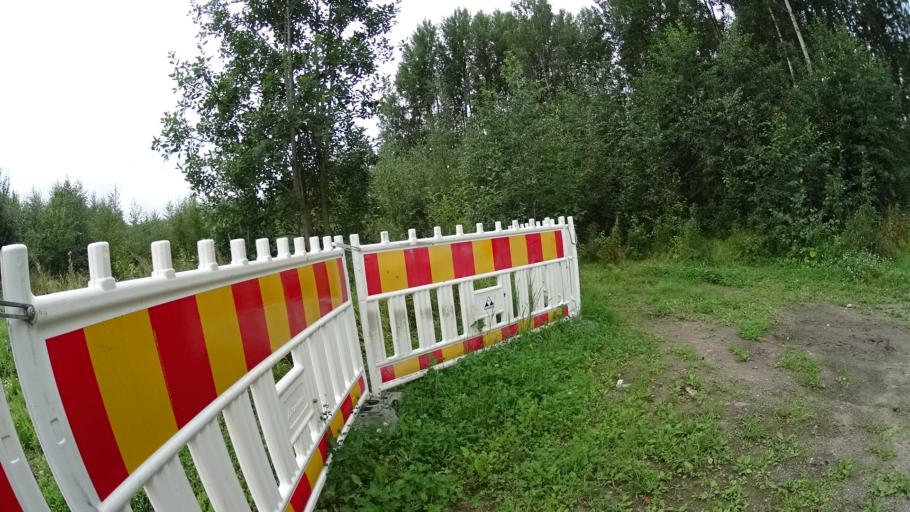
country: FI
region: Uusimaa
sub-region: Helsinki
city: Teekkarikylae
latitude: 60.2121
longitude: 24.8305
